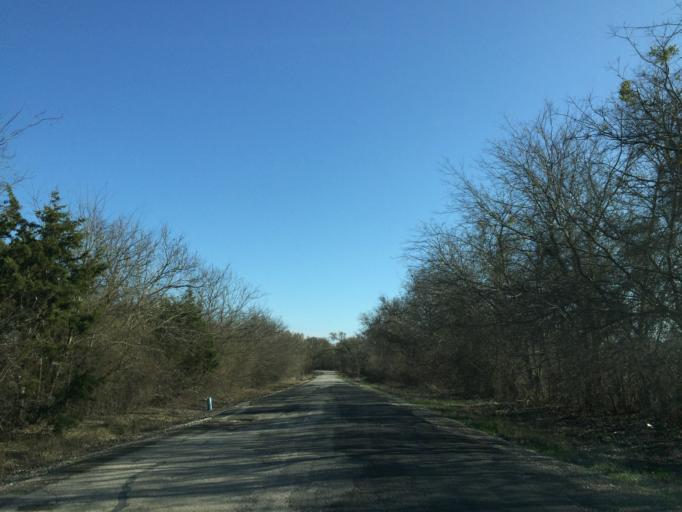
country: US
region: Texas
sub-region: Williamson County
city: Florence
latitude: 30.7738
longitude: -97.8382
